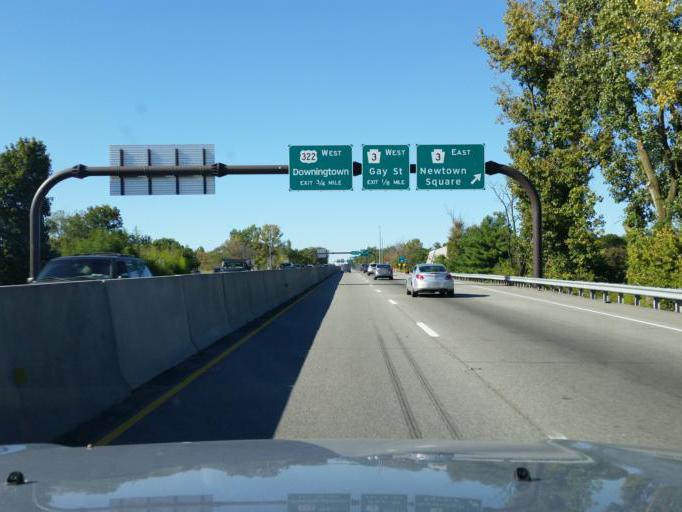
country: US
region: Pennsylvania
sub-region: Chester County
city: West Chester
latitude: 39.9647
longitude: -75.5808
